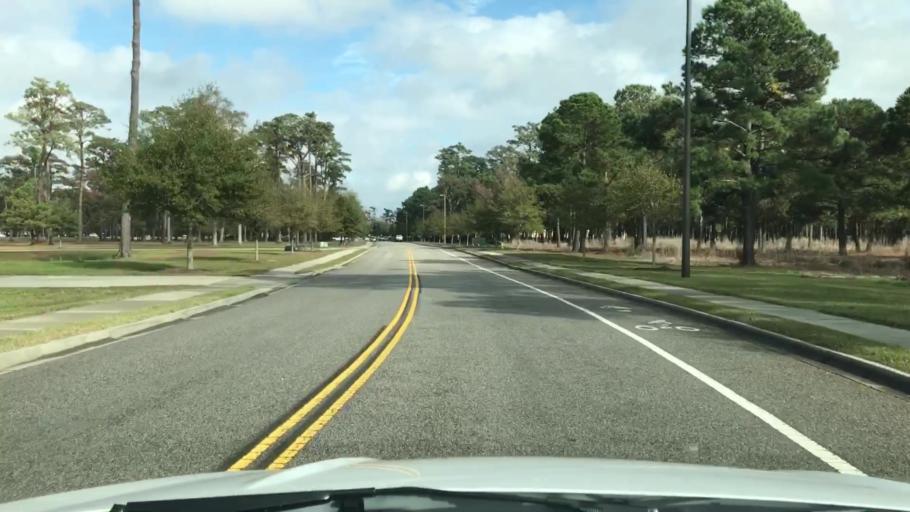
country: US
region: South Carolina
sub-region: Horry County
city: Myrtle Beach
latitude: 33.7228
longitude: -78.8755
